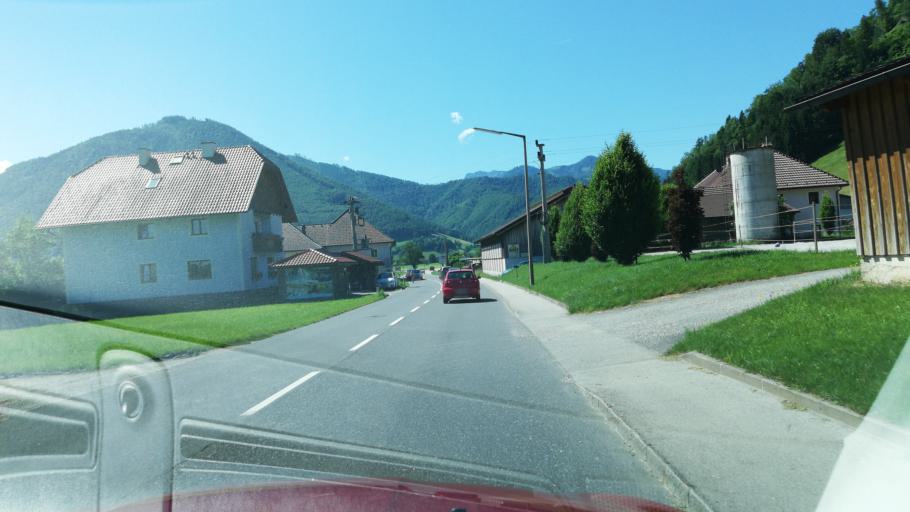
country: AT
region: Upper Austria
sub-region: Politischer Bezirk Kirchdorf an der Krems
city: Gruenburg
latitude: 47.8931
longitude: 14.2312
